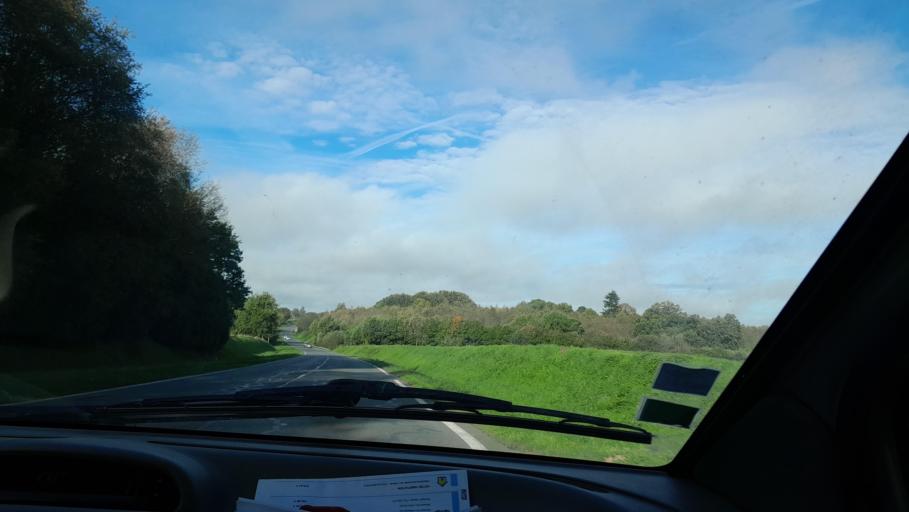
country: FR
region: Brittany
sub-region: Departement d'Ille-et-Vilaine
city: Saint-Germain-en-Cogles
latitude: 48.3783
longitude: -1.2583
